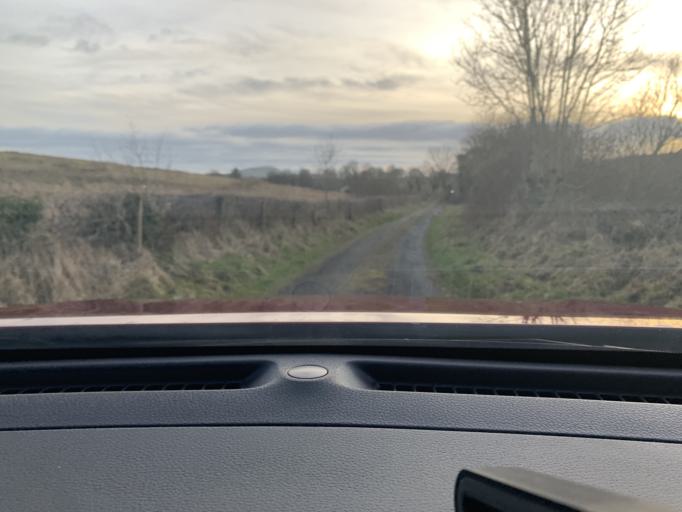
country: IE
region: Connaught
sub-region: Sligo
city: Strandhill
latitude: 54.1701
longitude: -8.6479
